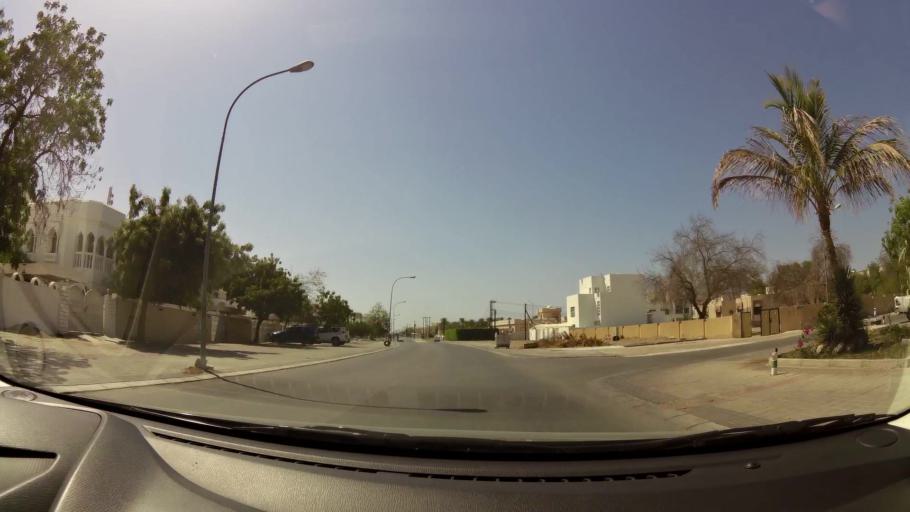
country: OM
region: Muhafazat Masqat
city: As Sib al Jadidah
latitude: 23.6294
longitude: 58.2188
